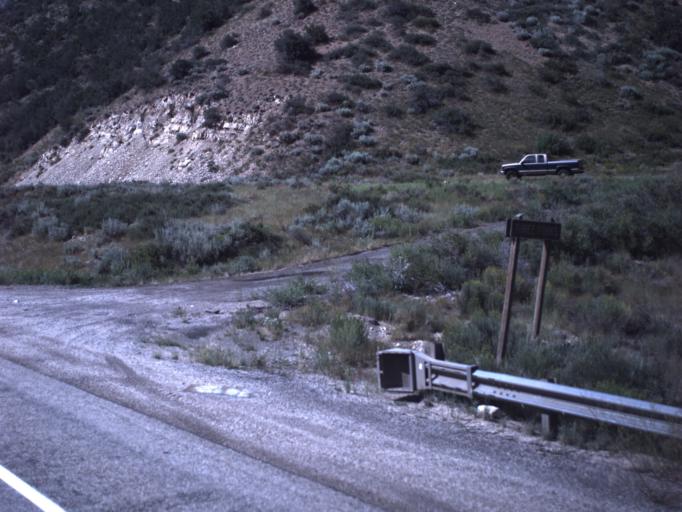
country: US
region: Utah
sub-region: Wasatch County
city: Heber
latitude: 40.3487
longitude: -111.2705
